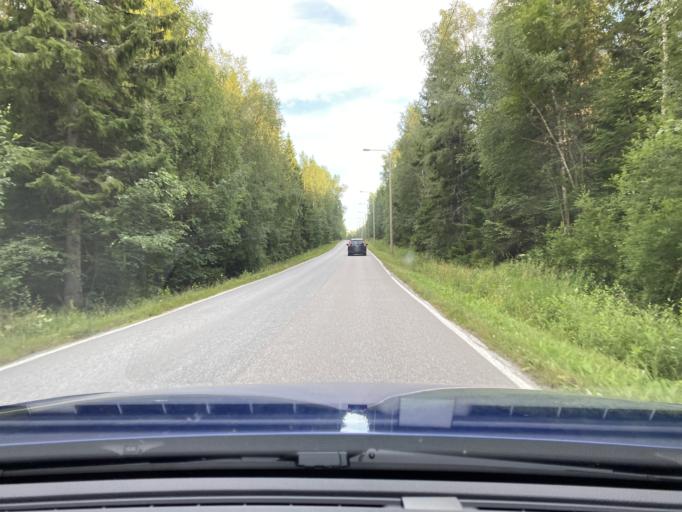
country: FI
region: Ostrobothnia
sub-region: Vaasa
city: Korsnaes
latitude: 62.9509
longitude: 21.1762
